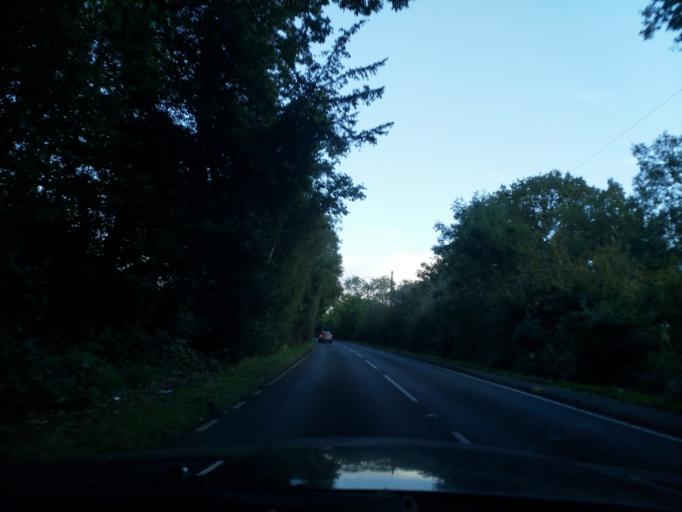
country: GB
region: England
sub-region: Solihull
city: Cheswick Green
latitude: 52.3488
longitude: -1.7732
